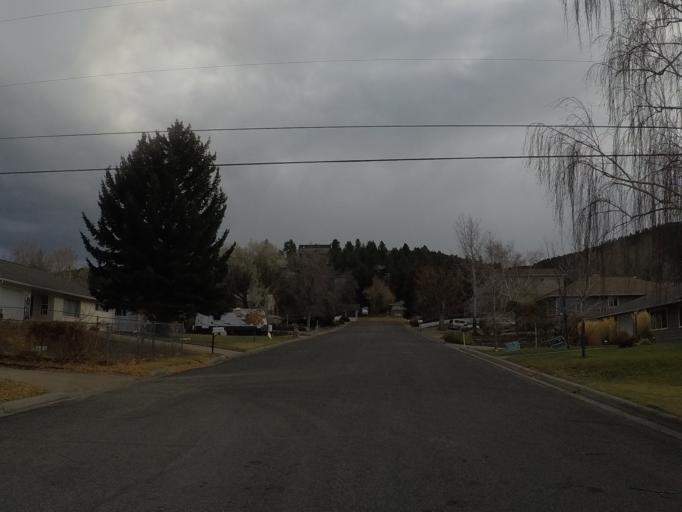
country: US
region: Montana
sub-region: Lewis and Clark County
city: Helena
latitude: 46.5828
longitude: -112.0190
